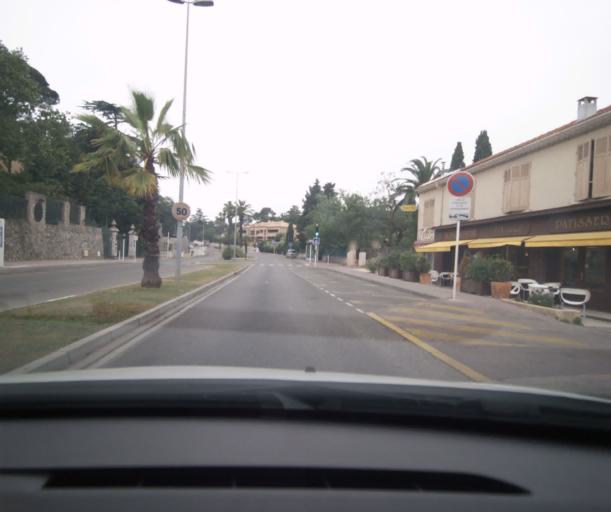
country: FR
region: Provence-Alpes-Cote d'Azur
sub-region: Departement du Var
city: La Valette-du-Var
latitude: 43.1097
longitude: 5.9800
